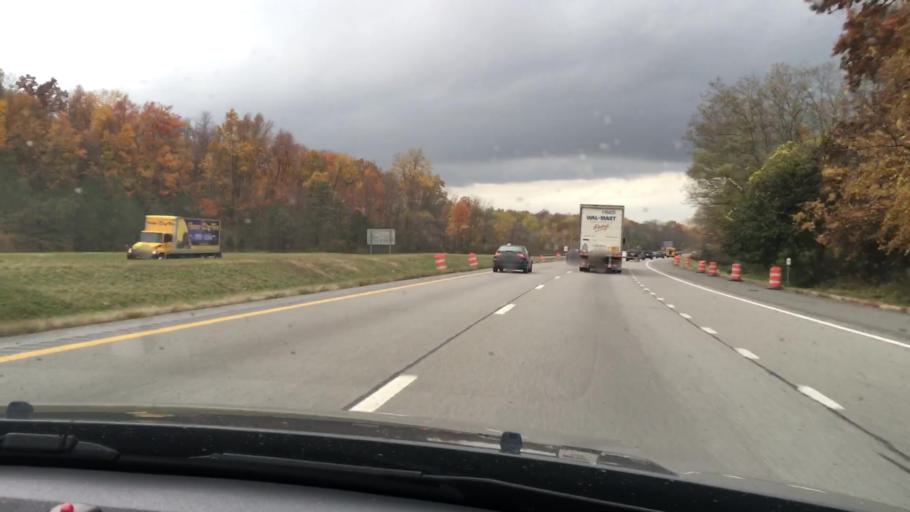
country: US
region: New York
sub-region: Dutchess County
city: Fishkill
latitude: 41.5227
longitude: -73.9042
